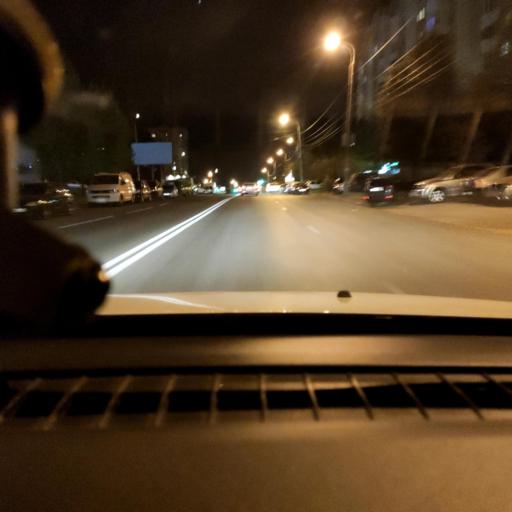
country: RU
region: Samara
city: Samara
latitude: 53.2653
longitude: 50.2151
